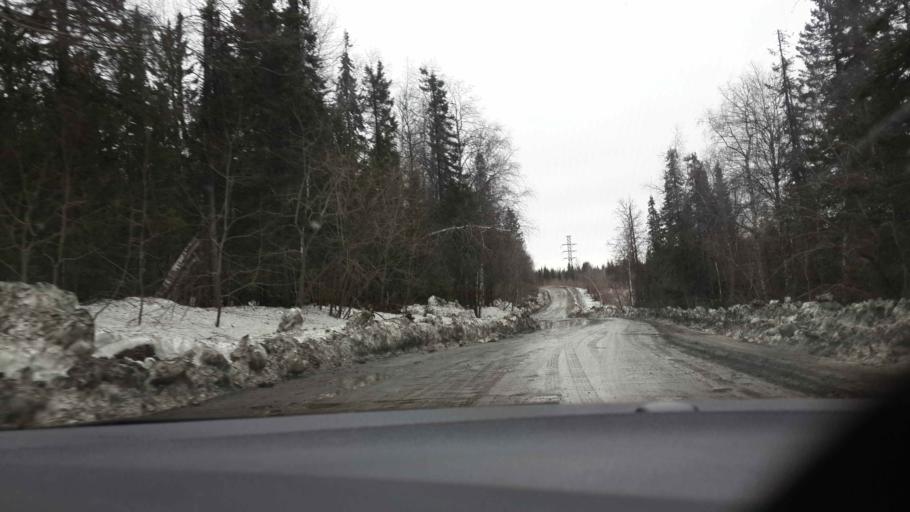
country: RU
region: Chelyabinsk
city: Magnitka
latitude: 55.2654
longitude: 59.6996
